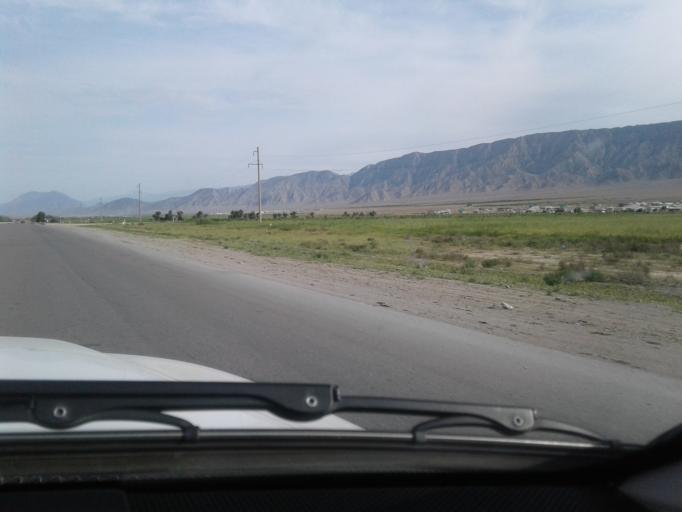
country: TM
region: Ahal
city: Arcabil
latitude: 38.2090
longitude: 57.8153
